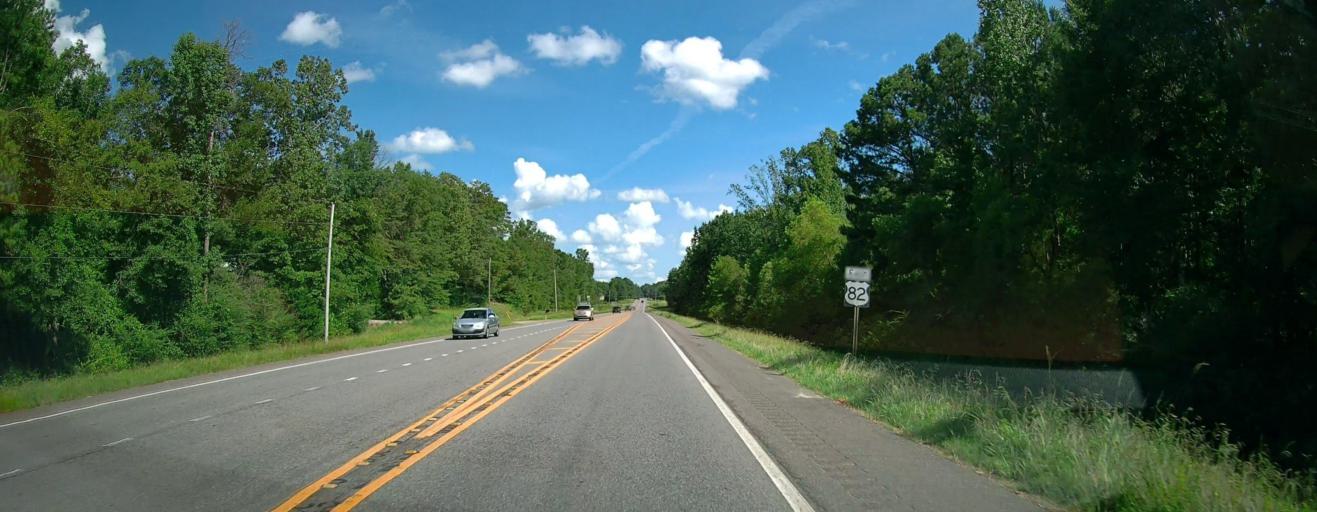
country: US
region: Alabama
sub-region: Pickens County
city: Gordo
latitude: 33.3028
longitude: -87.8829
